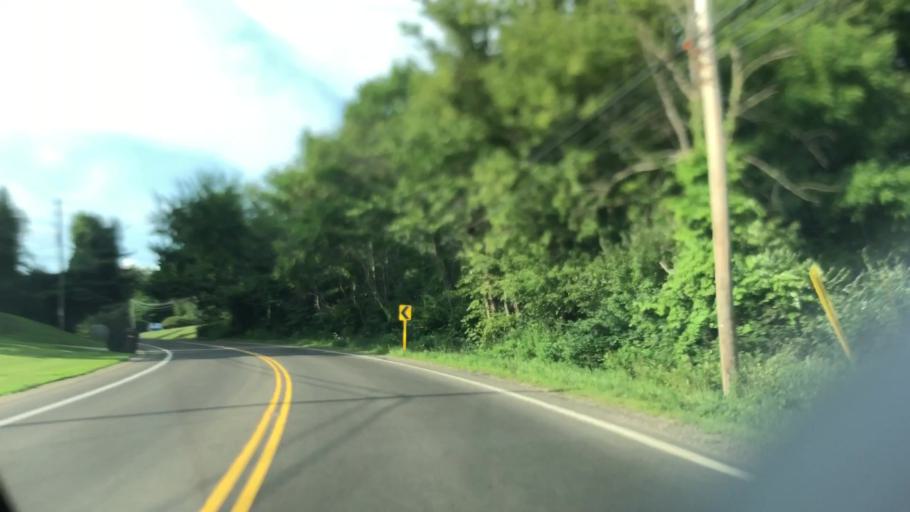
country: US
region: Ohio
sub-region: Summit County
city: Greensburg
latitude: 40.8696
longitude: -81.4805
